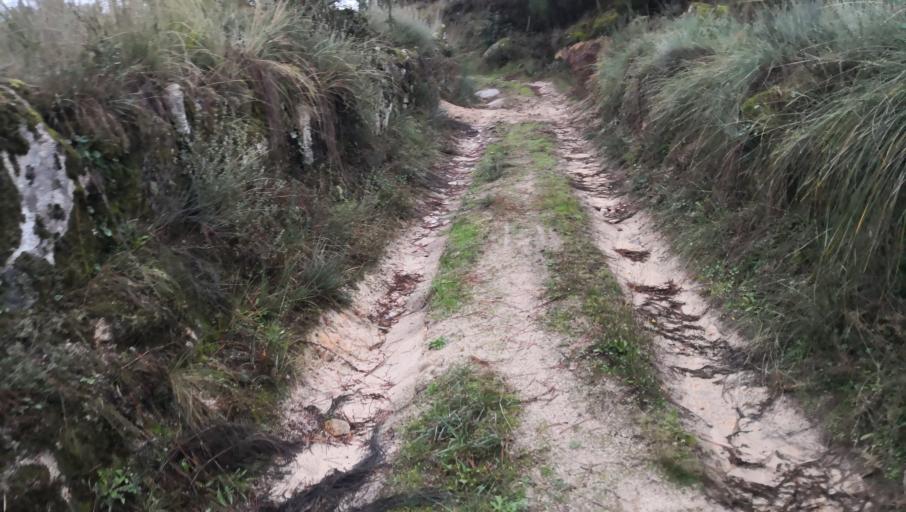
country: PT
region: Vila Real
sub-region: Vila Real
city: Vila Real
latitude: 41.2830
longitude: -7.7485
